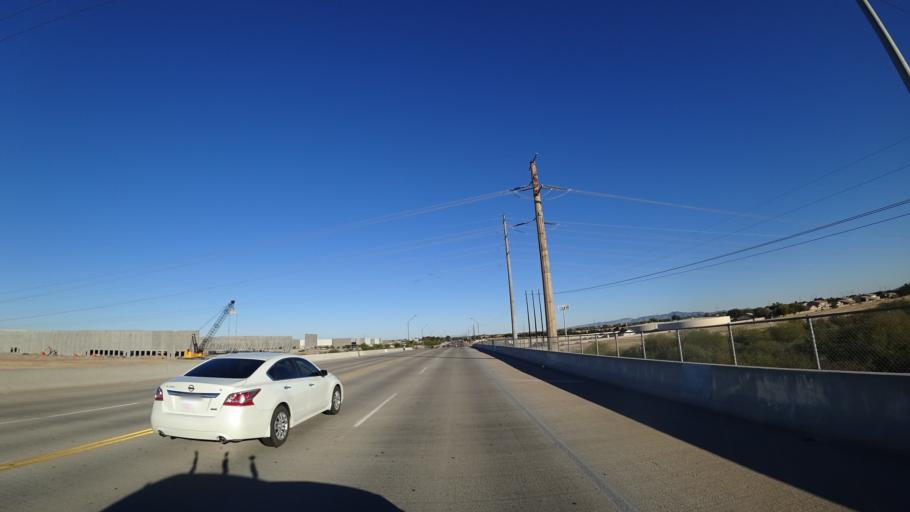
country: US
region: Arizona
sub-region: Maricopa County
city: Avondale
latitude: 33.4496
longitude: -112.3324
